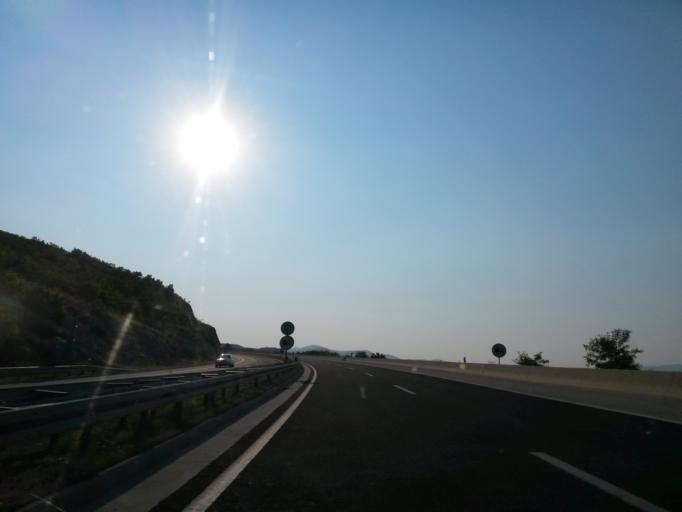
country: HR
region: Splitsko-Dalmatinska
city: Greda
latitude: 43.5815
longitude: 16.6607
